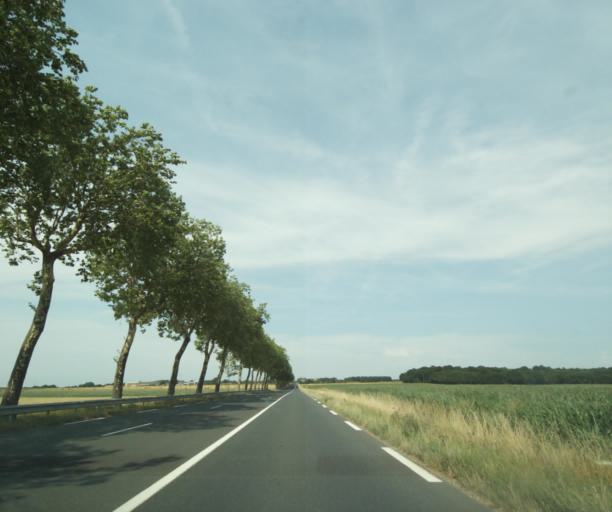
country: FR
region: Centre
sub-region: Departement d'Indre-et-Loire
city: Sainte-Maure-de-Touraine
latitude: 47.1260
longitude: 0.6280
